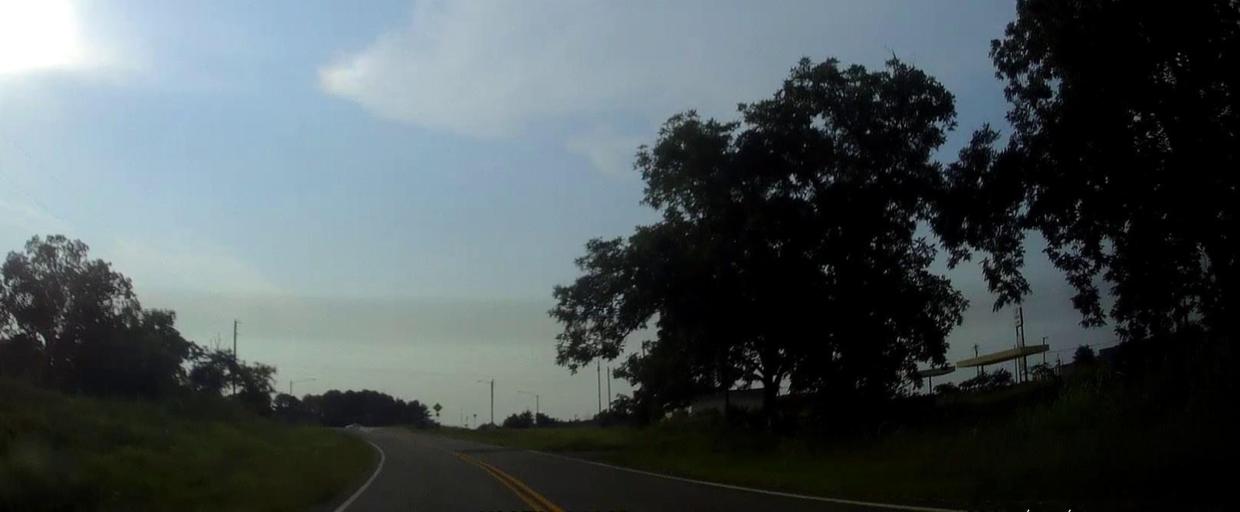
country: US
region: Georgia
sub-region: Laurens County
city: Dublin
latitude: 32.4927
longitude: -82.9832
